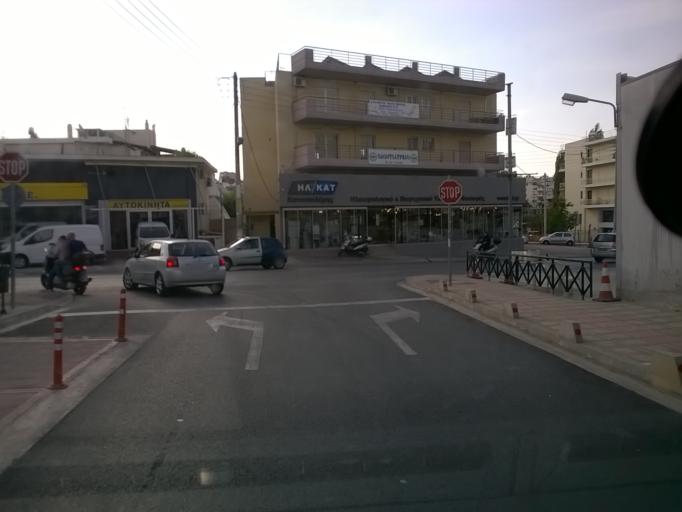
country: GR
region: Attica
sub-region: Nomarchia Athinas
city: Agios Dimitrios
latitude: 37.9306
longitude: 23.7268
